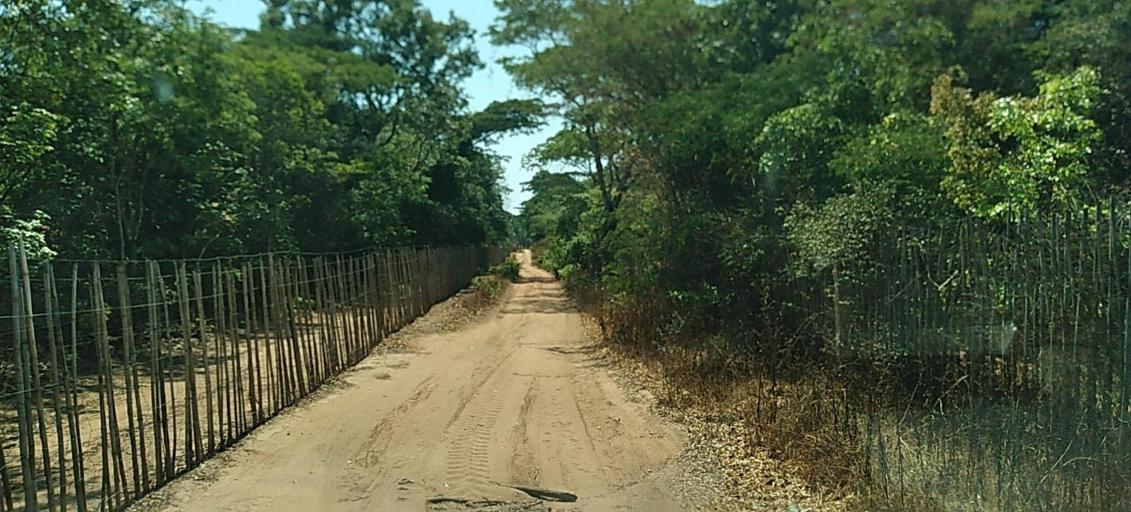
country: ZM
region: Copperbelt
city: Luanshya
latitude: -13.0090
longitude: 28.4595
